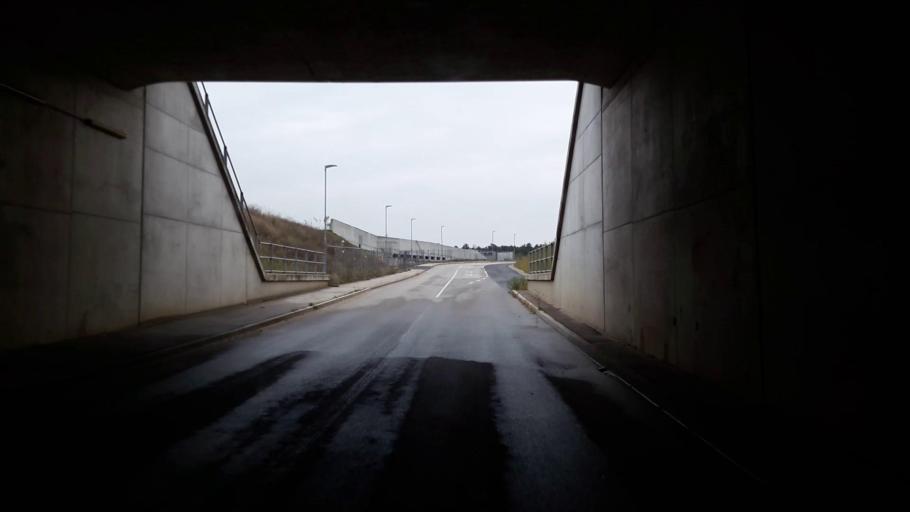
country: AT
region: Lower Austria
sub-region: Politischer Bezirk Ganserndorf
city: Strasshof an der Nordbahn
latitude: 48.3223
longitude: 16.6505
